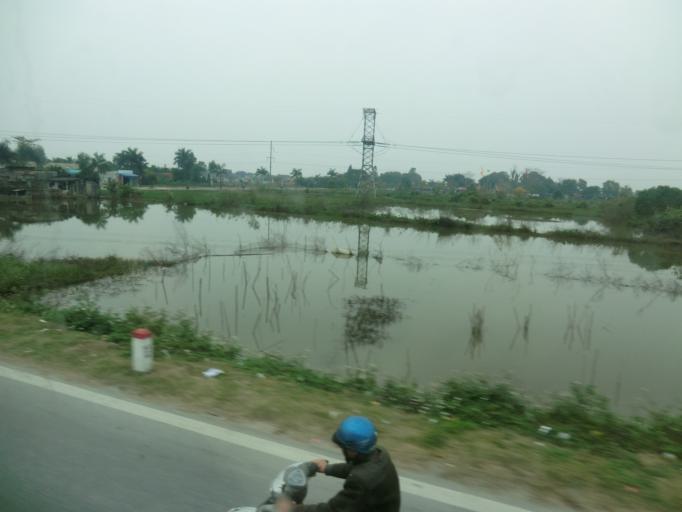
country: VN
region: Nam Dinh
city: Thanh Pho Nam Dinh
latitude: 20.4512
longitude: 106.1650
